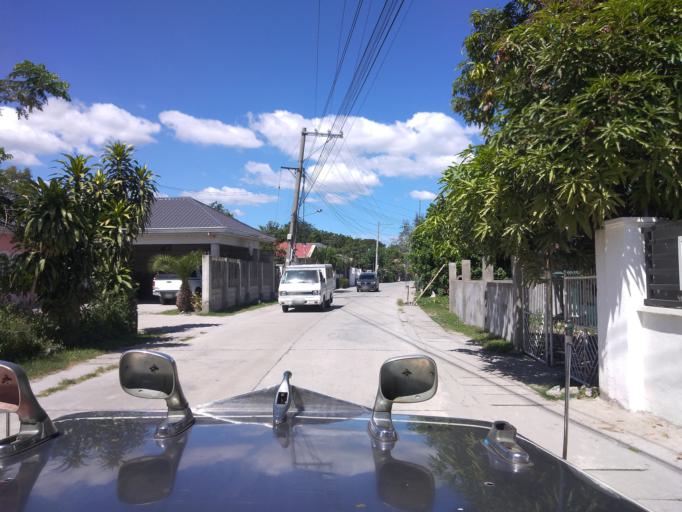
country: PH
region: Central Luzon
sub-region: Province of Pampanga
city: Magliman
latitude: 15.0355
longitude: 120.6469
